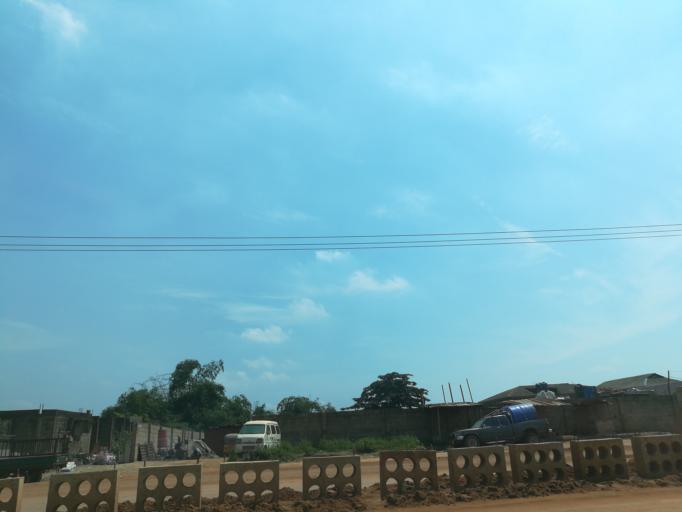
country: NG
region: Lagos
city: Ikorodu
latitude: 6.6579
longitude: 3.4749
